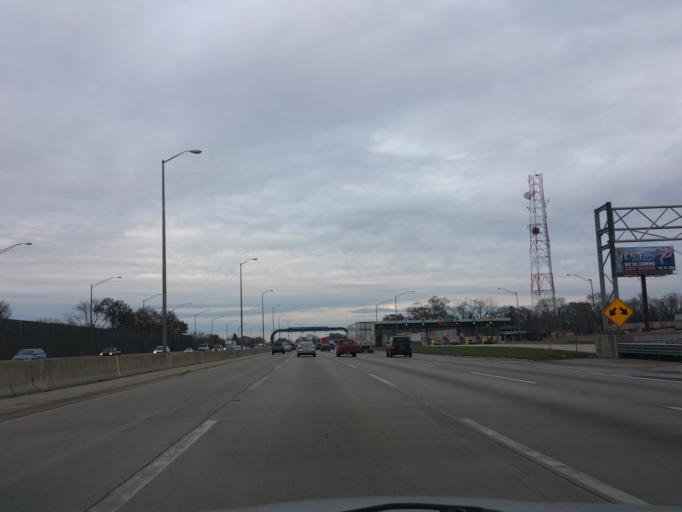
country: US
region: Illinois
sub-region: Cook County
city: Justice
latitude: 41.7427
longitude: -87.8354
